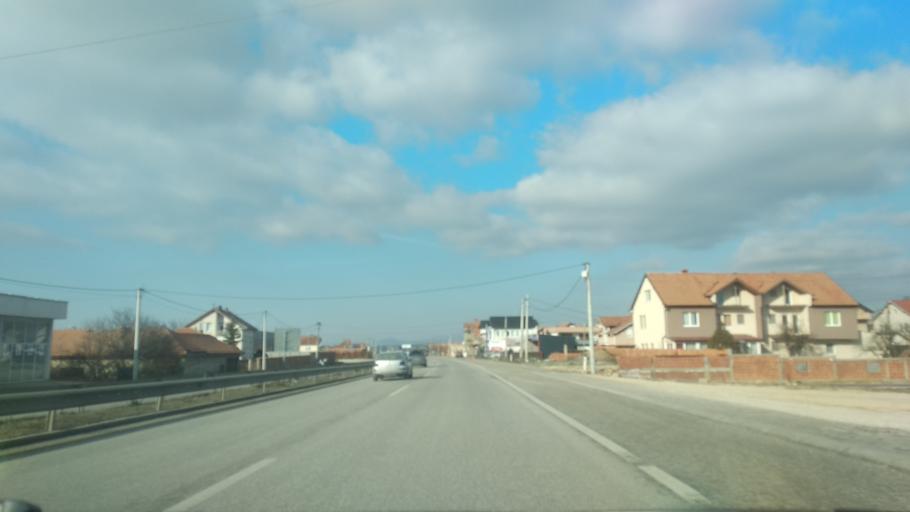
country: XK
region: Pristina
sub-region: Komuna e Obiliqit
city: Obiliq
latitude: 42.7058
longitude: 21.1066
